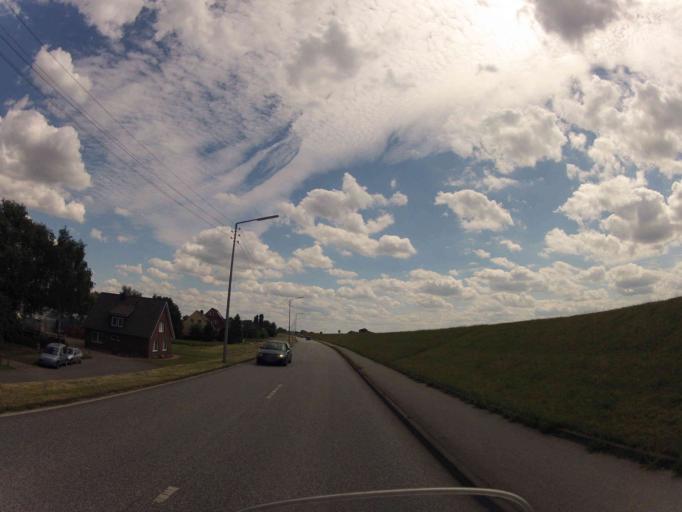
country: DE
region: Hamburg
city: Rothenburgsort
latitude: 53.4857
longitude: 10.0543
